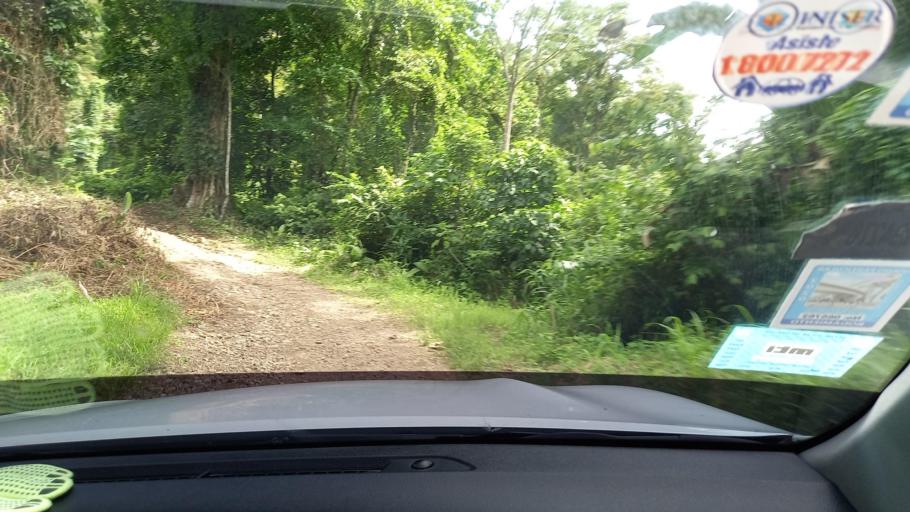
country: NI
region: Jinotega
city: San Jose de Bocay
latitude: 13.3987
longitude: -85.6978
